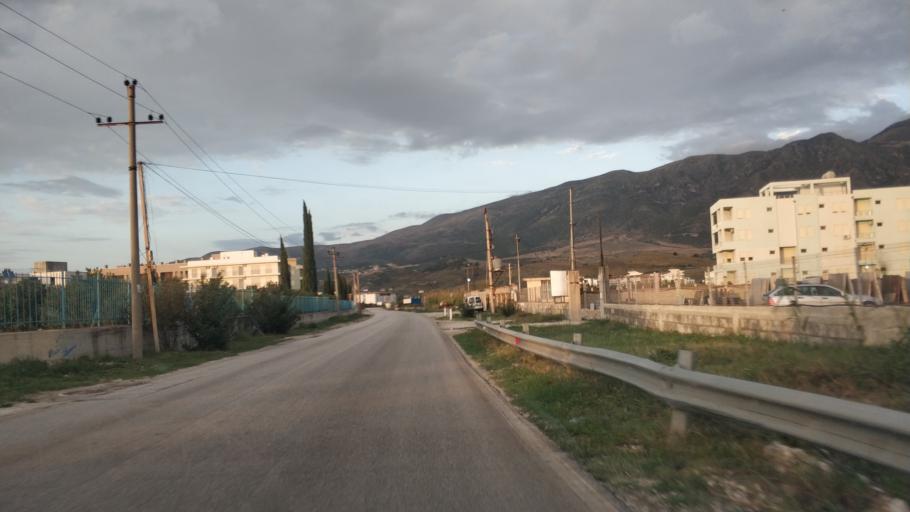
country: AL
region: Vlore
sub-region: Rrethi i Vlores
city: Orikum
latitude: 40.3378
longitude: 19.4754
